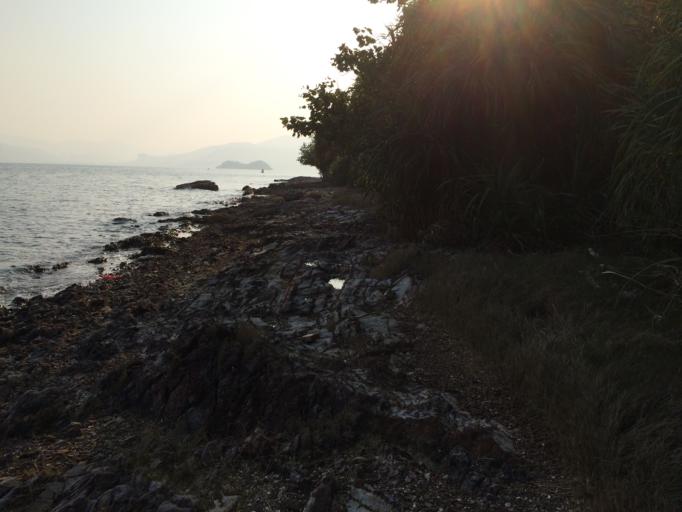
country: HK
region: Tai Po
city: Tai Po
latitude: 22.4541
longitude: 114.2328
